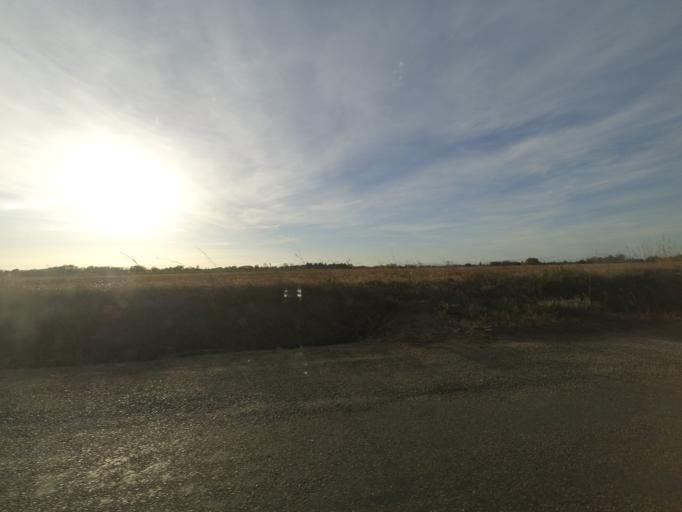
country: FR
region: Languedoc-Roussillon
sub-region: Departement du Gard
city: Le Cailar
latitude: 43.6890
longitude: 4.2314
